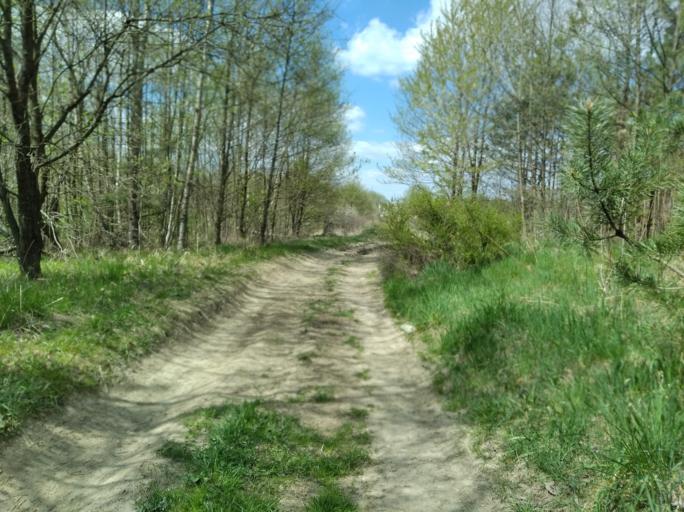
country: PL
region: Subcarpathian Voivodeship
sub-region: Powiat brzozowski
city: Wesola
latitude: 49.7484
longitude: 22.0798
